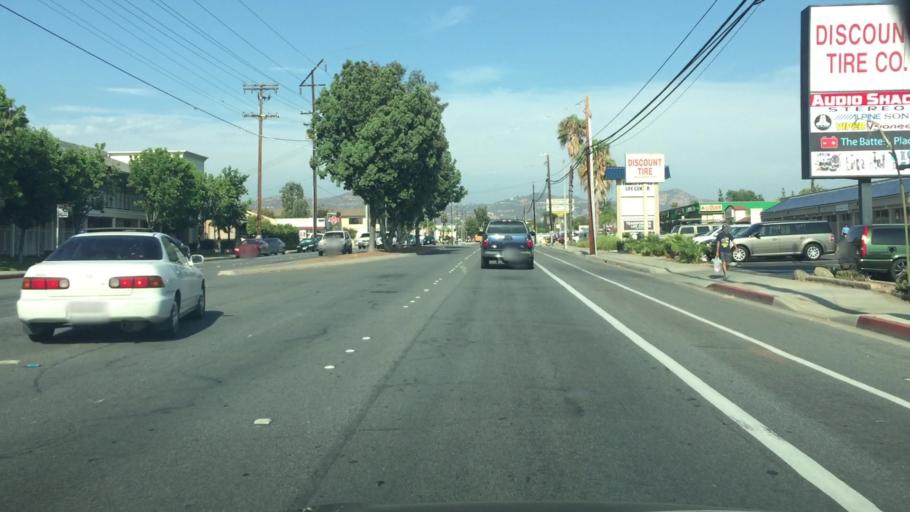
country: US
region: California
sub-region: San Diego County
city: Bostonia
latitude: 32.8077
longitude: -116.9482
